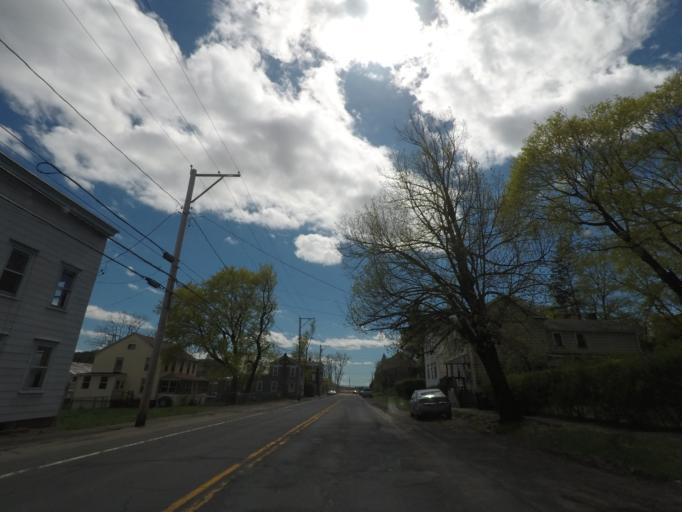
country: US
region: New York
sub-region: Greene County
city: Athens
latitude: 42.2588
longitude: -73.8100
